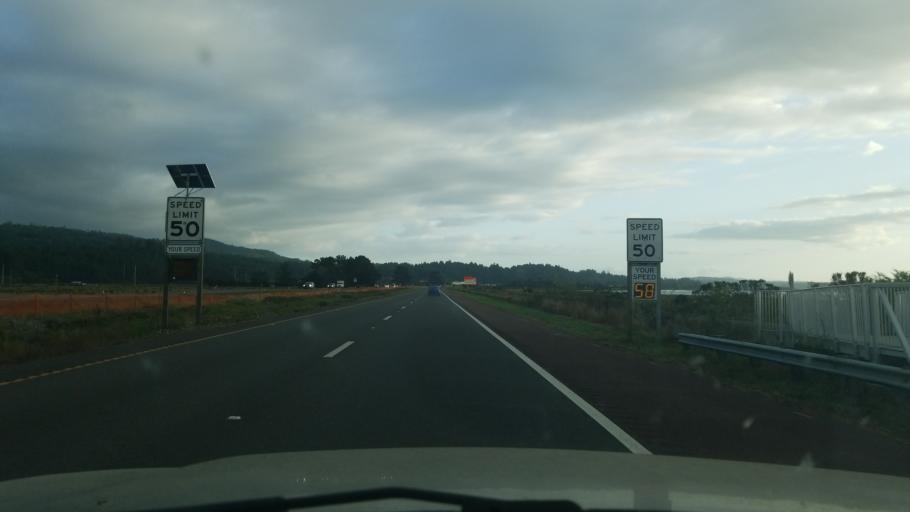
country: US
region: California
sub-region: Humboldt County
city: Bayside
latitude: 40.8406
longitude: -124.0822
